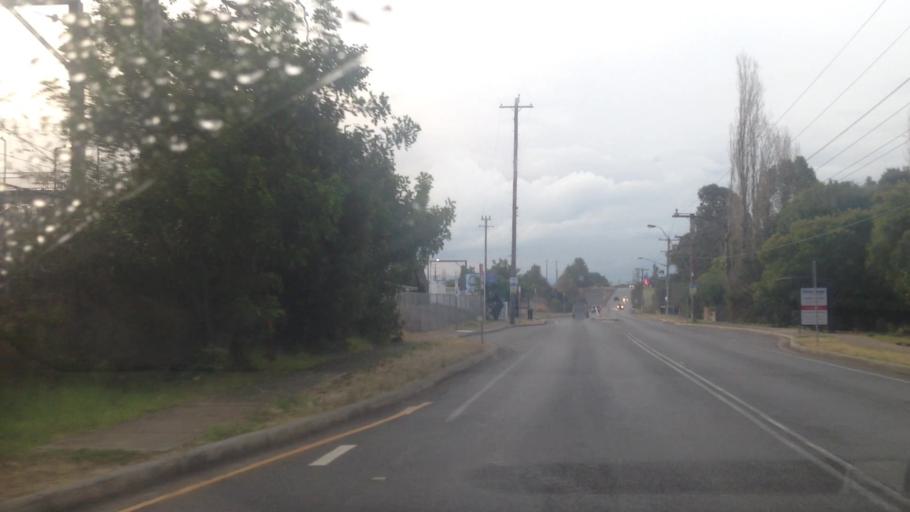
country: AU
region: New South Wales
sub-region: Wyong Shire
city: Charmhaven
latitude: -33.1805
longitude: 151.4874
